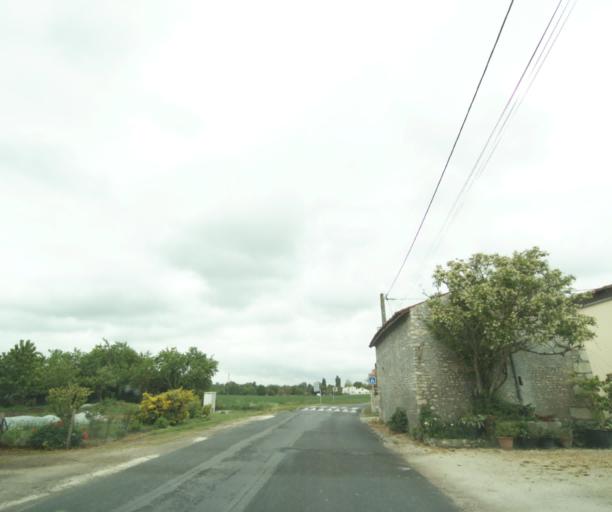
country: FR
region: Poitou-Charentes
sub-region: Departement de la Charente-Maritime
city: Chaniers
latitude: 45.6966
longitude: -0.5215
